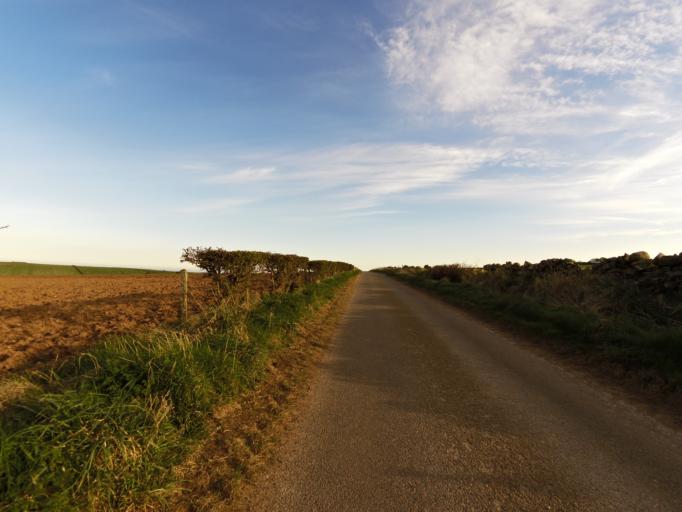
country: GB
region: Scotland
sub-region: Aberdeenshire
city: Inverbervie
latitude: 56.8824
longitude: -2.2365
